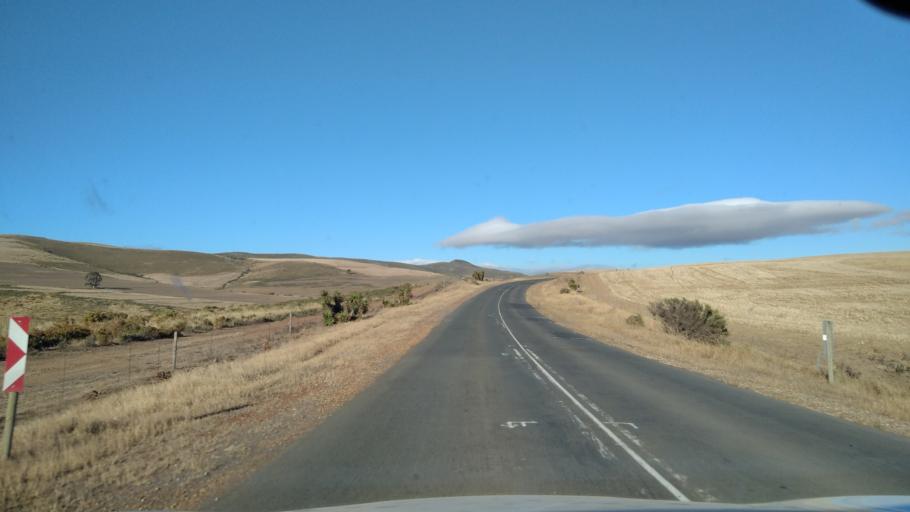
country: ZA
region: Western Cape
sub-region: Overberg District Municipality
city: Caledon
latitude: -34.1678
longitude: 19.2916
